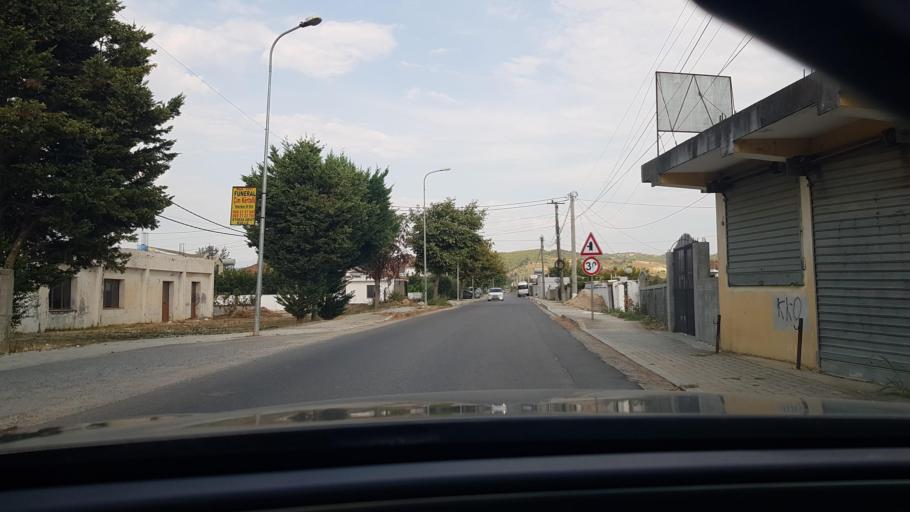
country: AL
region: Durres
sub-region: Rrethi i Durresit
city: Manze
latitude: 41.4744
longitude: 19.5500
